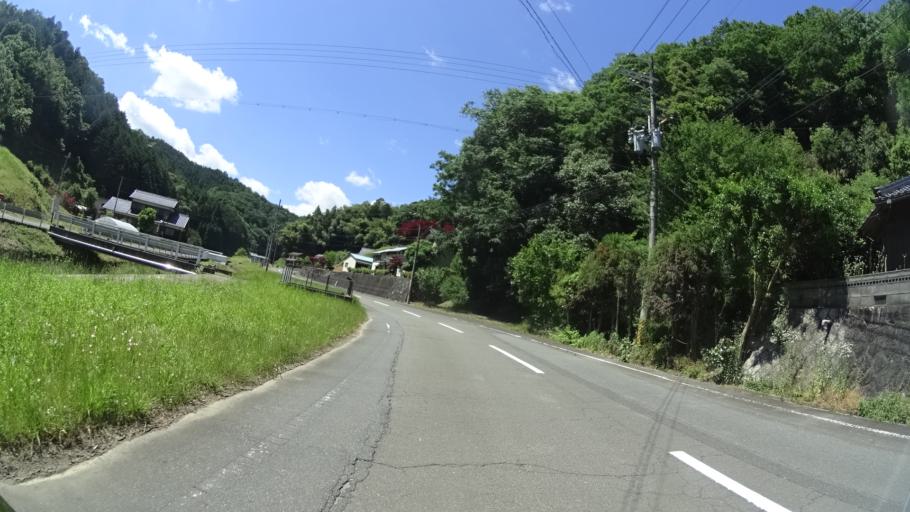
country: JP
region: Kyoto
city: Miyazu
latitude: 35.4143
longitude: 135.1882
